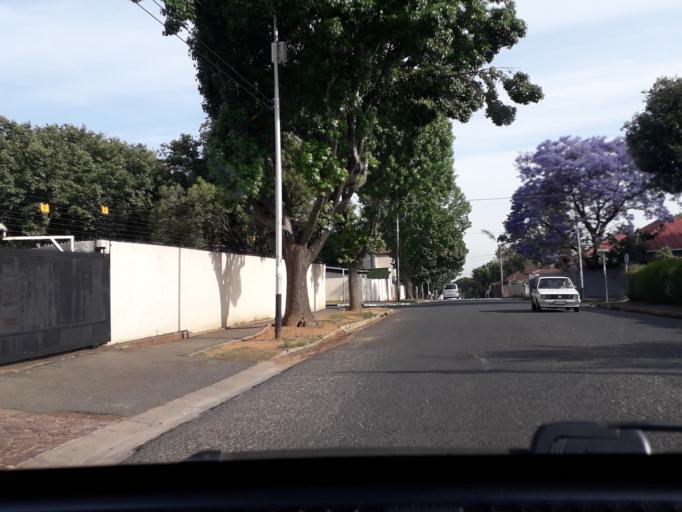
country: ZA
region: Gauteng
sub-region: City of Johannesburg Metropolitan Municipality
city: Johannesburg
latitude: -26.1424
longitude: 28.0892
